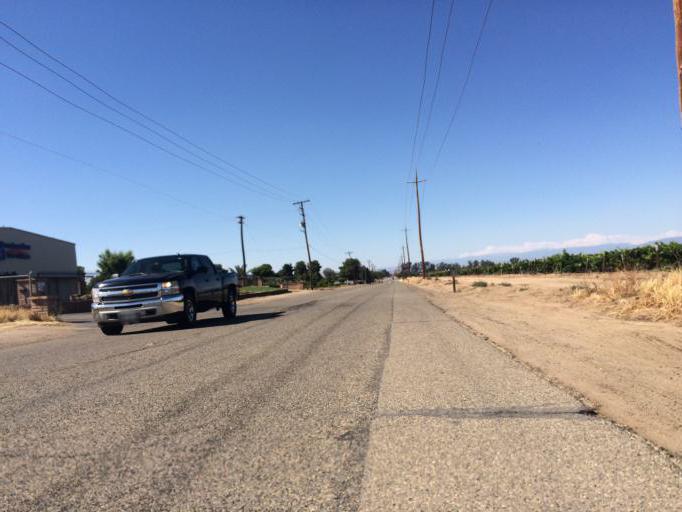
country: US
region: California
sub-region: Fresno County
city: Sanger
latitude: 36.7586
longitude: -119.6102
